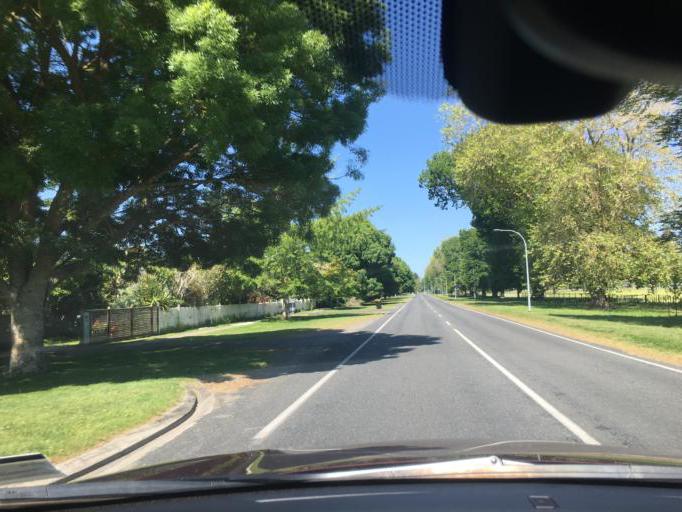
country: NZ
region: Waikato
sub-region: Waipa District
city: Cambridge
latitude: -37.9156
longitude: 175.4628
